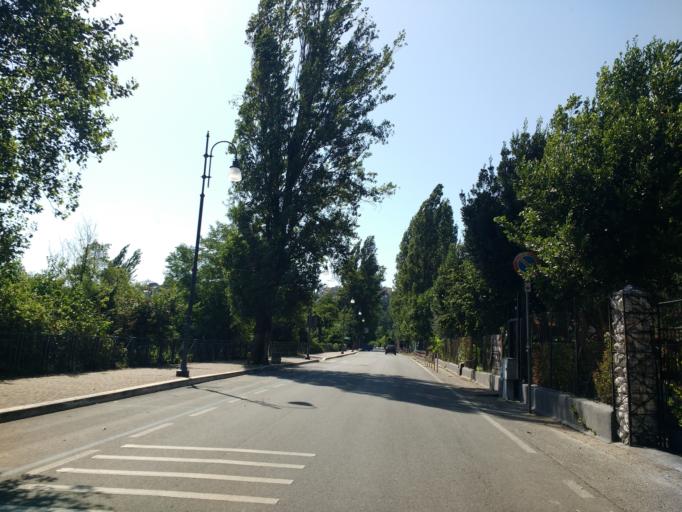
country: IT
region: Latium
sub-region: Citta metropolitana di Roma Capitale
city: Castel Gandolfo
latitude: 41.7612
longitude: 12.6620
